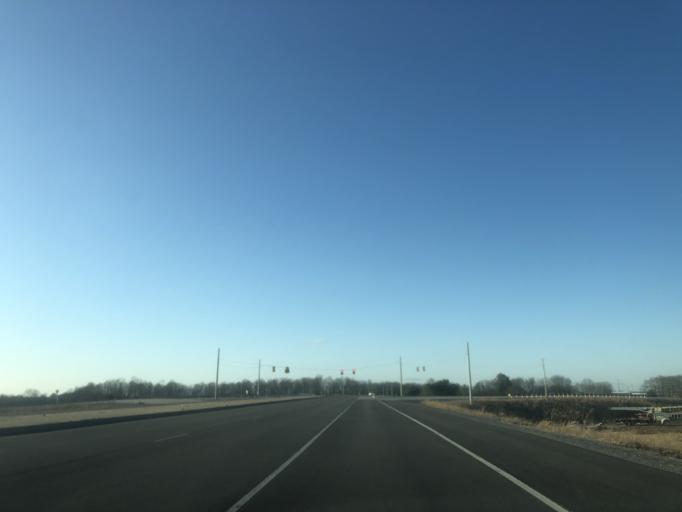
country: US
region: Tennessee
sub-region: Sumner County
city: Portland
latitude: 36.6291
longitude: -86.5711
